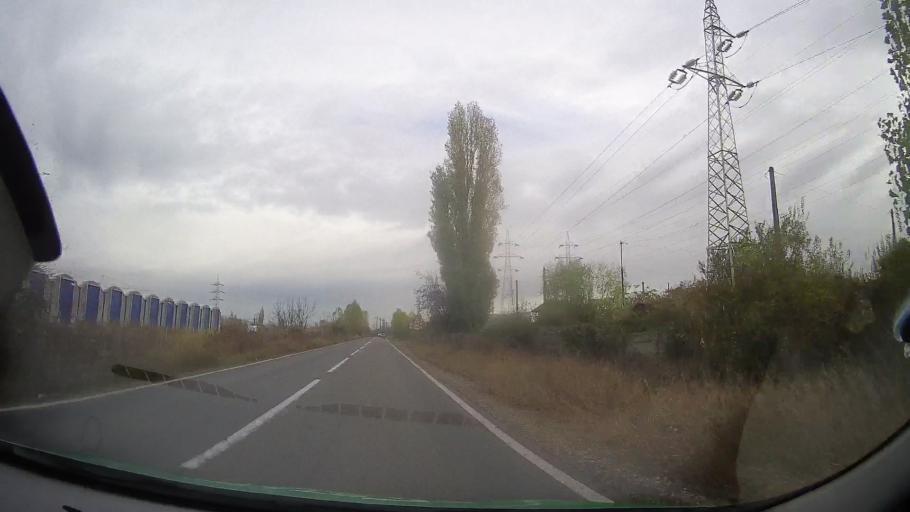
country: RO
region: Prahova
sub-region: Comuna Bucov
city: Bucov
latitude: 44.9542
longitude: 26.0832
